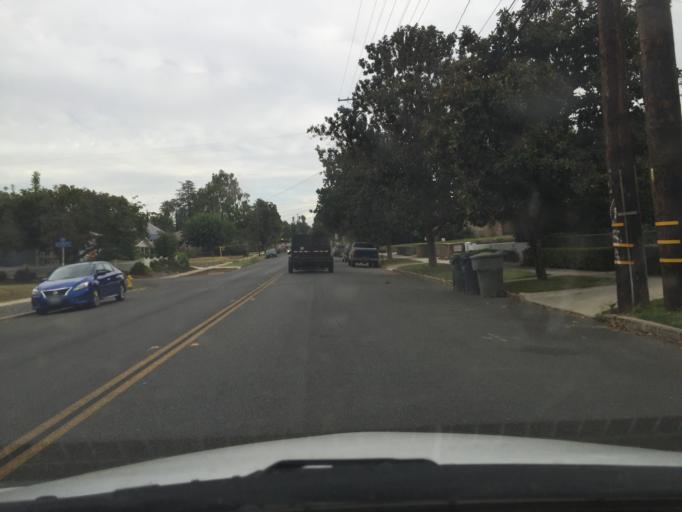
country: US
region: California
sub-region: San Bernardino County
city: Redlands
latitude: 34.0513
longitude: -117.1900
